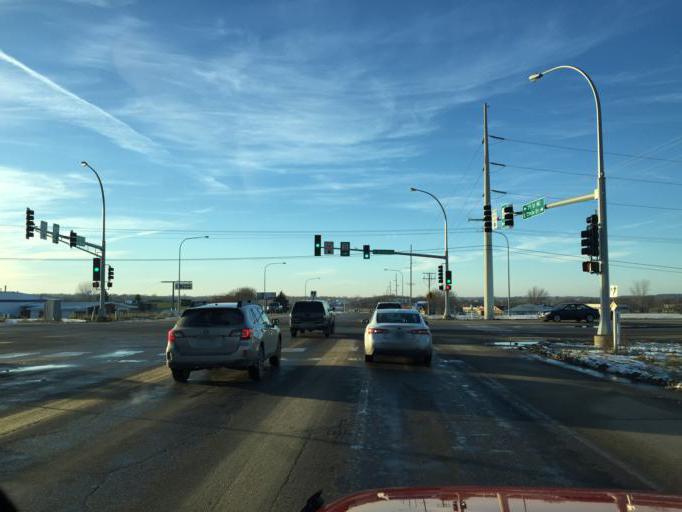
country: US
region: Minnesota
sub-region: Olmsted County
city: Rochester
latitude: 44.0588
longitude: -92.4532
